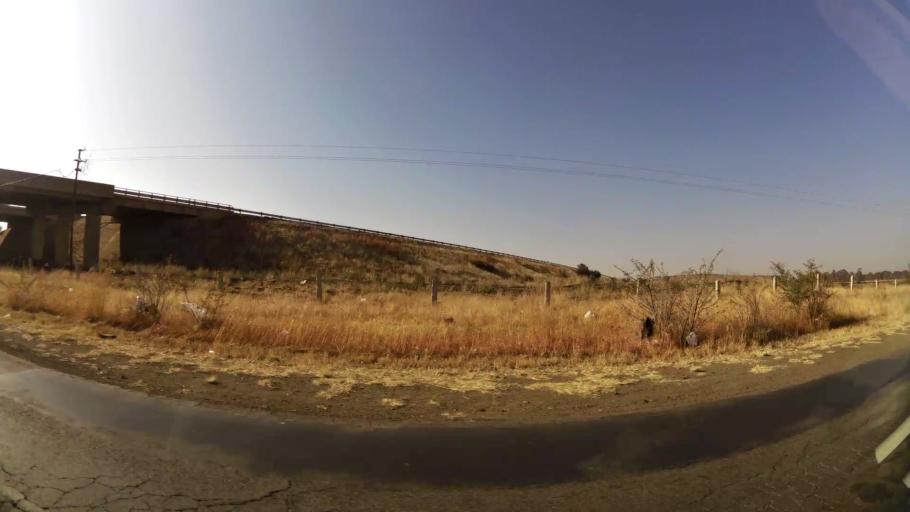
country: ZA
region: Orange Free State
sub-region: Mangaung Metropolitan Municipality
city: Bloemfontein
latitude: -29.1809
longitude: 26.1894
